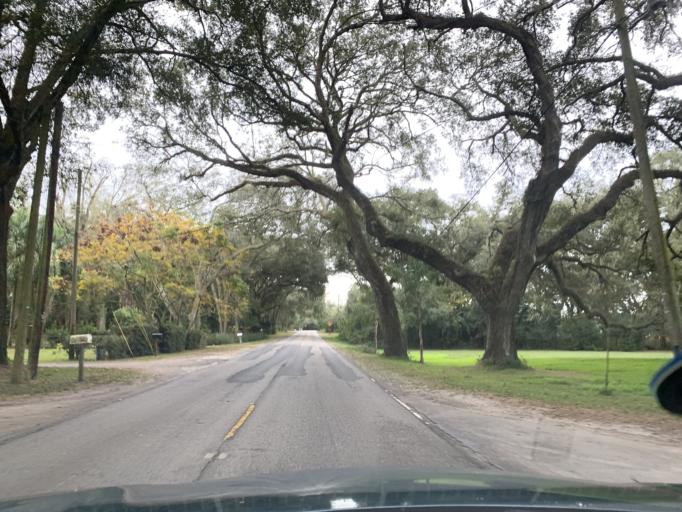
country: US
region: Florida
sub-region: Pasco County
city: Zephyrhills North
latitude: 28.2859
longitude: -82.1811
